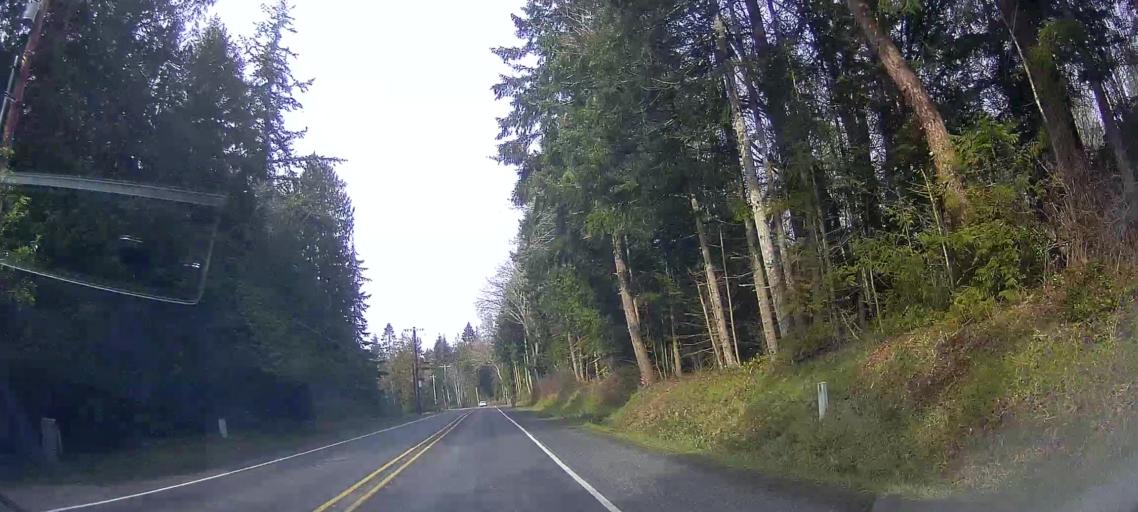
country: US
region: Washington
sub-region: Island County
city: Camano
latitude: 48.1332
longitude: -122.4643
